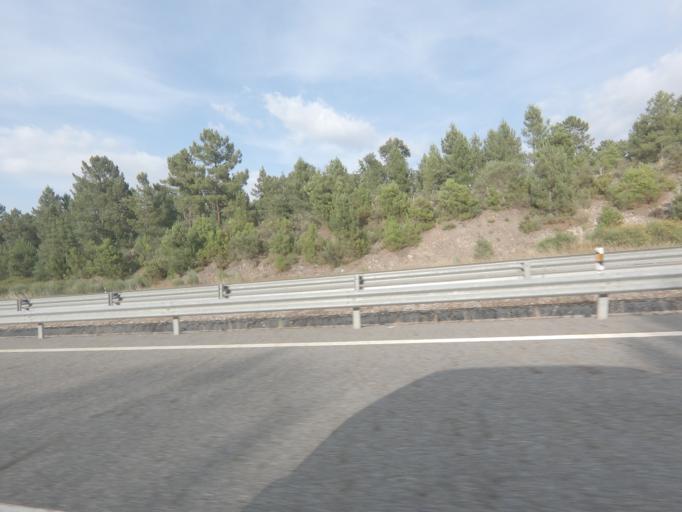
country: PT
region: Vila Real
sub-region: Chaves
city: Chaves
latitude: 41.7210
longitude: -7.5433
